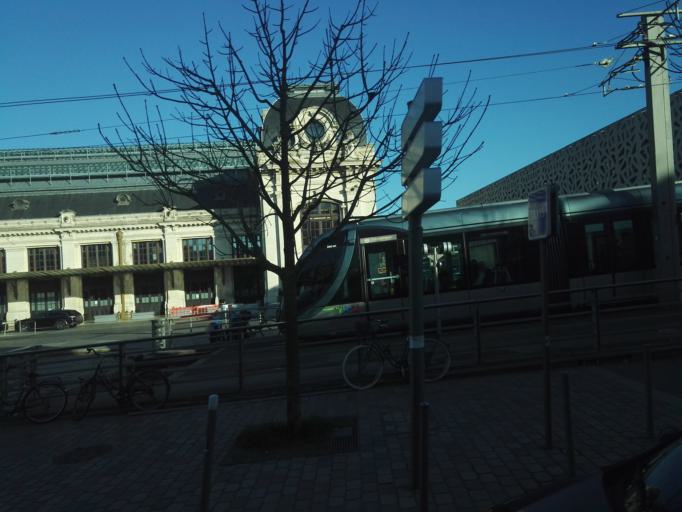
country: FR
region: Aquitaine
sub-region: Departement de la Gironde
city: Begles
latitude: 44.8248
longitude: -0.5574
